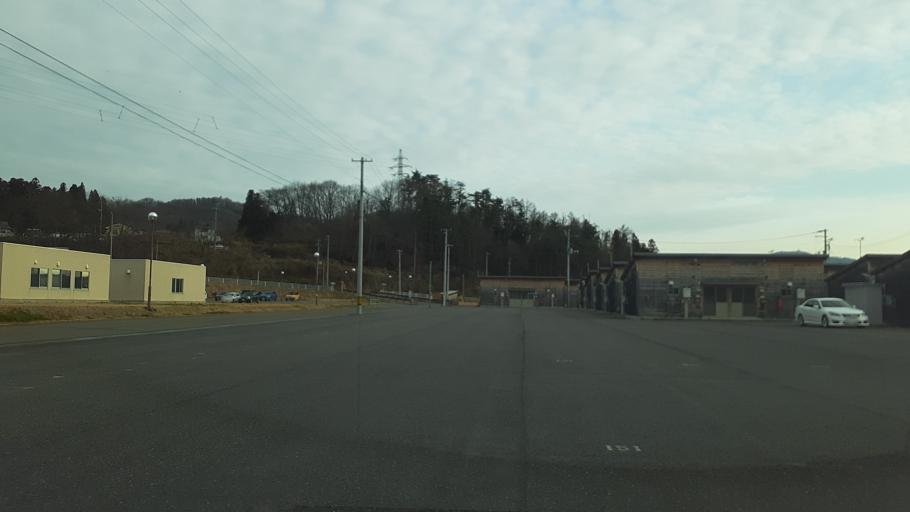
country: JP
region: Fukushima
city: Kitakata
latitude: 37.5230
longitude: 139.9515
